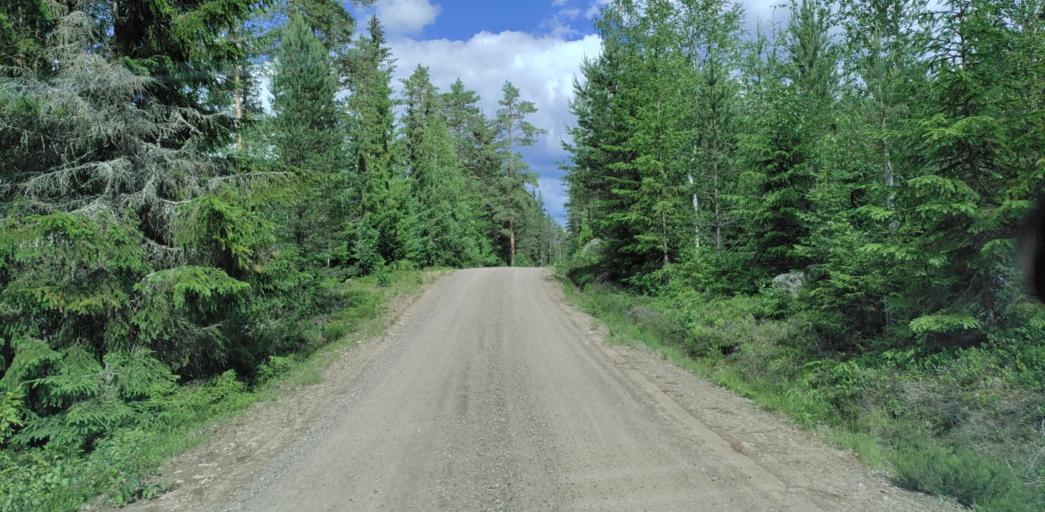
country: SE
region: Vaermland
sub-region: Hagfors Kommun
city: Ekshaerad
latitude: 60.0780
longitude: 13.2916
